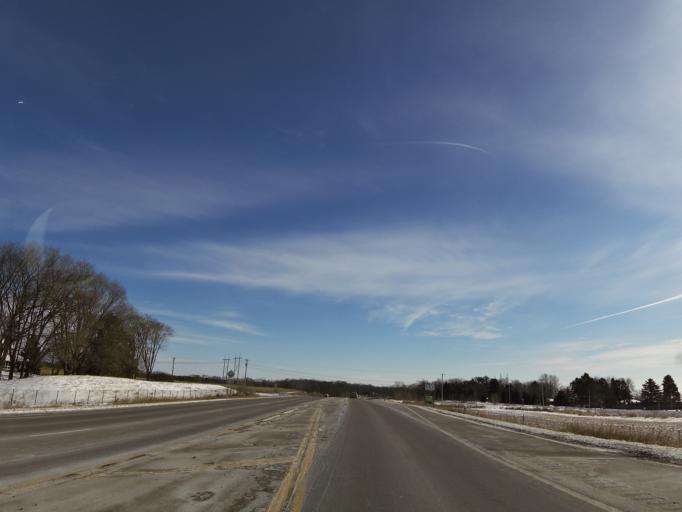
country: US
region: Minnesota
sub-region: Dakota County
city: Hastings
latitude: 44.7560
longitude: -92.8347
